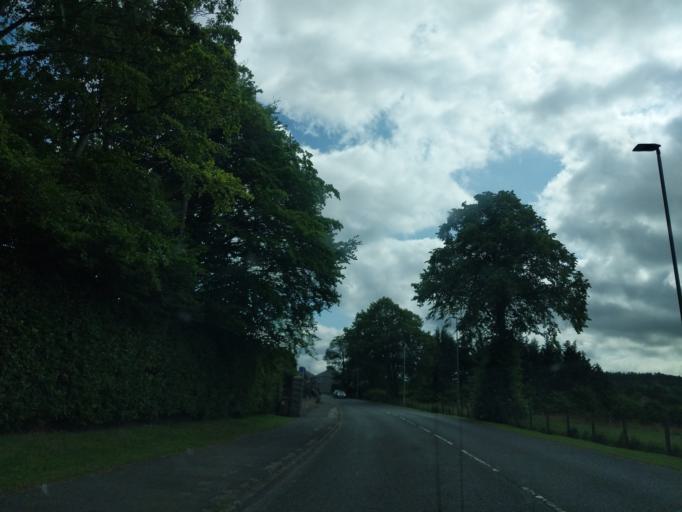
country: GB
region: Scotland
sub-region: Moray
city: Dufftown
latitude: 57.4507
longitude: -3.1310
